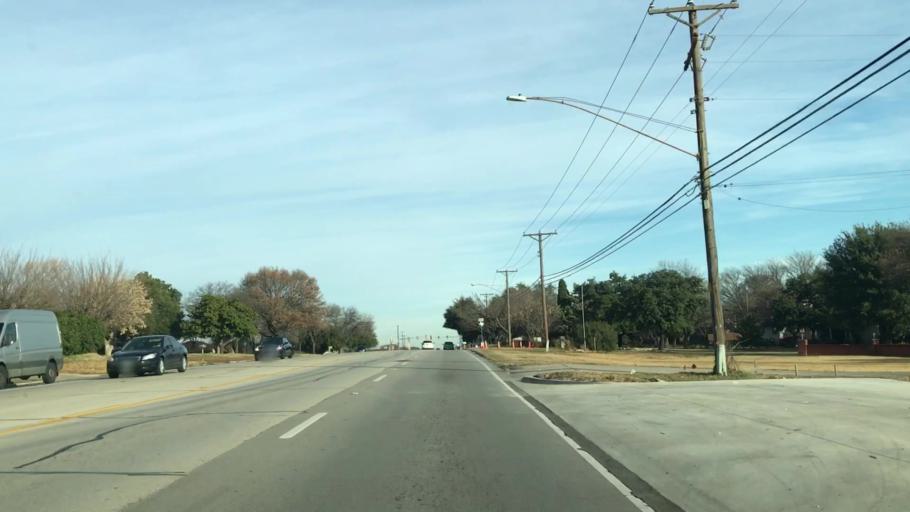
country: US
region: Texas
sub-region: Tarrant County
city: Sansom Park
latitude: 32.8188
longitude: -97.4199
